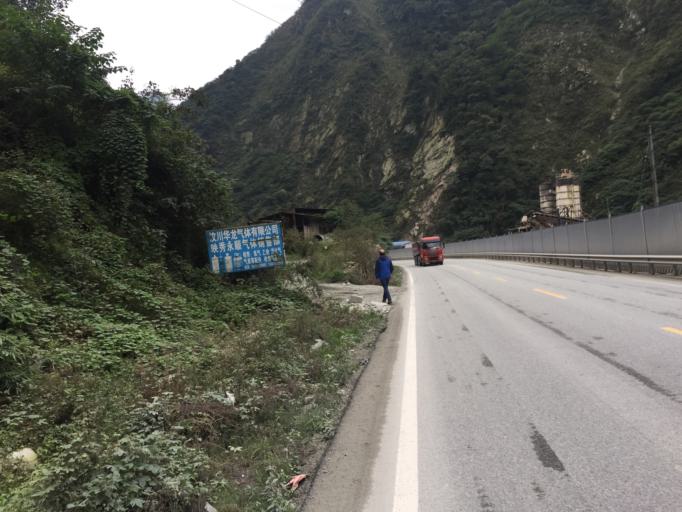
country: CN
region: Sichuan
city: Guangsheng
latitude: 31.0671
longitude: 103.4778
